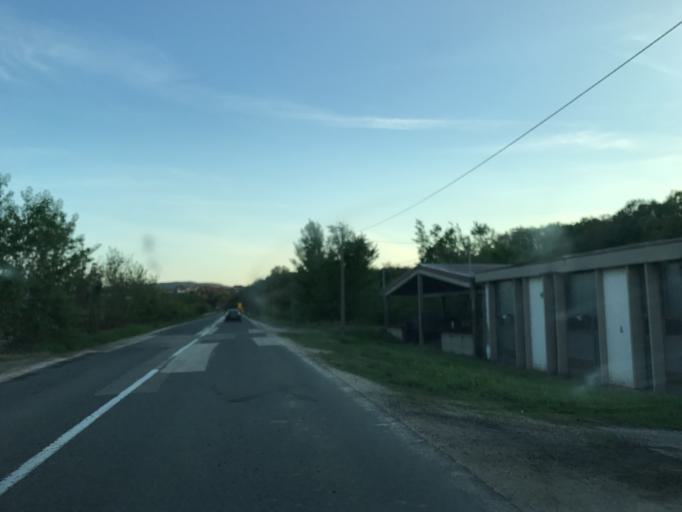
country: RO
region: Mehedinti
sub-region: Comuna Gogosu
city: Ostrovu Mare
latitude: 44.4784
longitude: 22.4529
